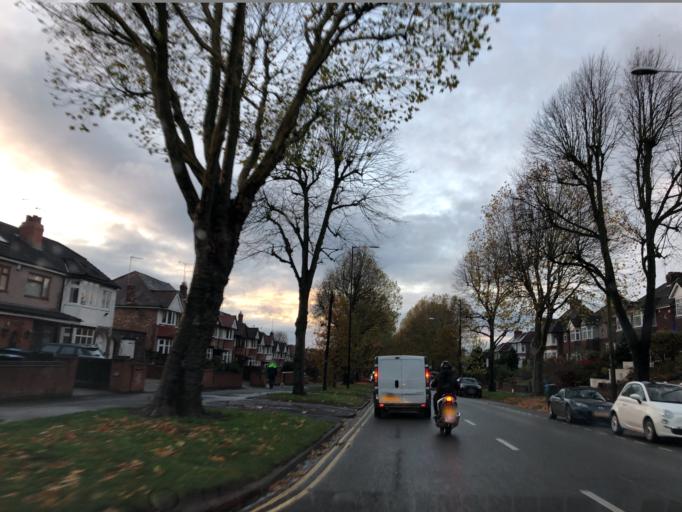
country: GB
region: England
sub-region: Coventry
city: Coventry
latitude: 52.4165
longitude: -1.5391
